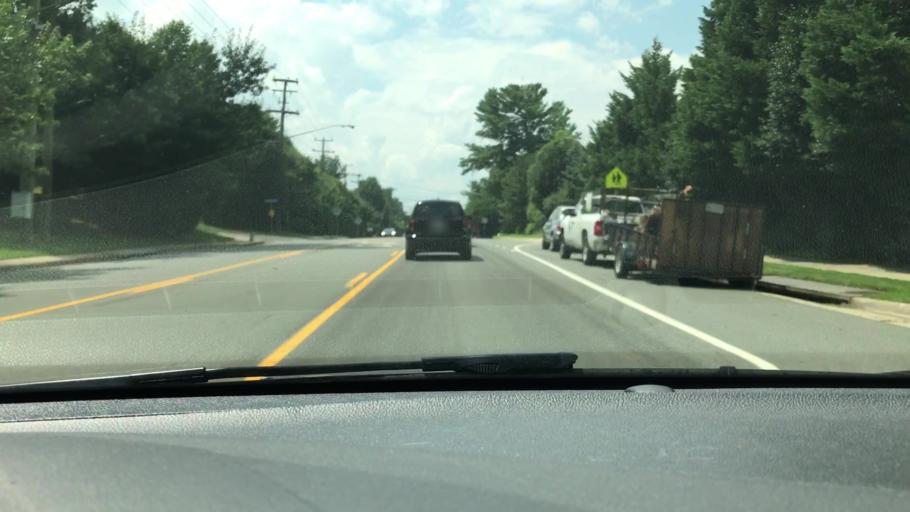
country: US
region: Virginia
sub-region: Fairfax County
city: McLean
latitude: 38.9121
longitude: -77.1708
